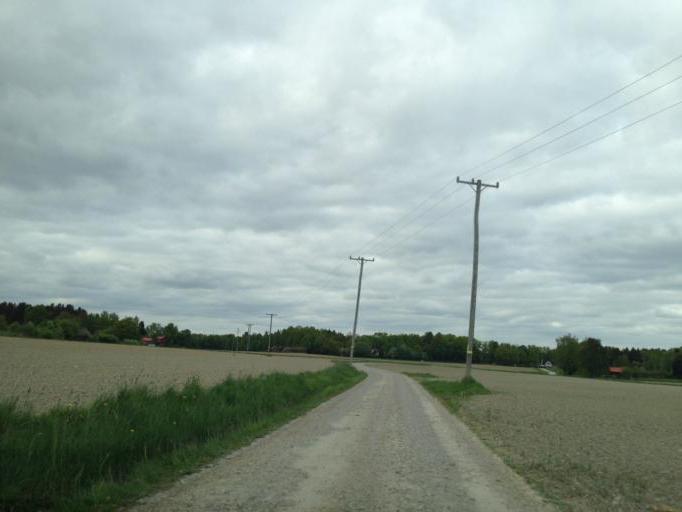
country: SE
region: Soedermanland
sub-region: Eskilstuna Kommun
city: Kvicksund
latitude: 59.4409
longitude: 16.3034
